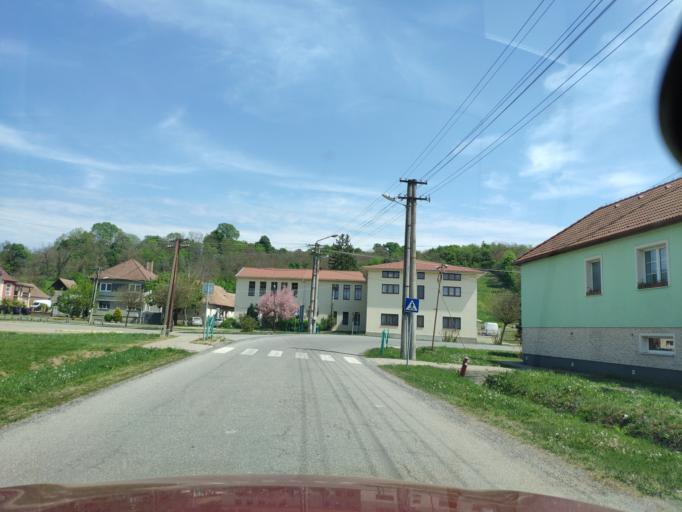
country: SK
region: Banskobystricky
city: Rimavska Sobota
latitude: 48.4477
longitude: 20.1158
